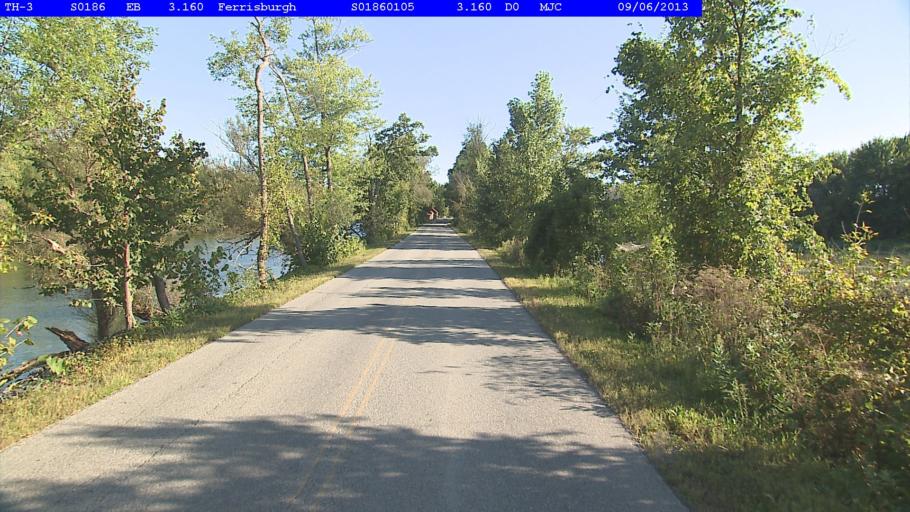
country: US
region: Vermont
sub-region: Addison County
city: Vergennes
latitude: 44.1810
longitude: -73.3090
